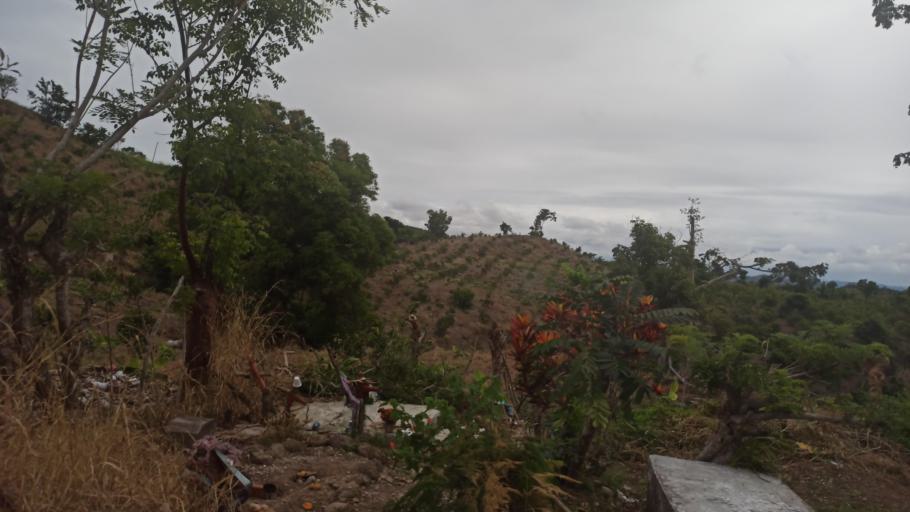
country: MX
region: Veracruz
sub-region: Papantla
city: Residencial Tajin
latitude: 20.6091
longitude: -97.3534
